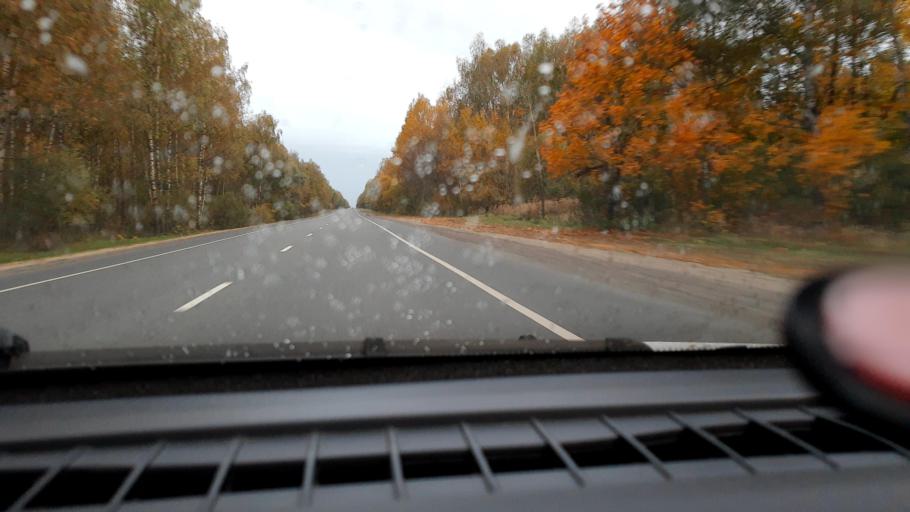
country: RU
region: Vladimir
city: Orgtrud
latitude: 56.2044
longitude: 40.7377
